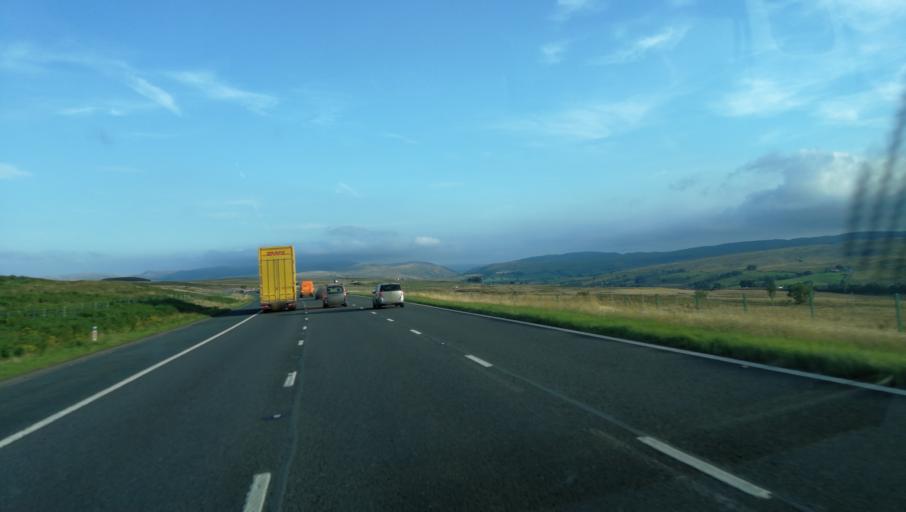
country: GB
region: England
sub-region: Cumbria
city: Appleby-in-Westmorland
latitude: 54.4905
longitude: -2.6408
